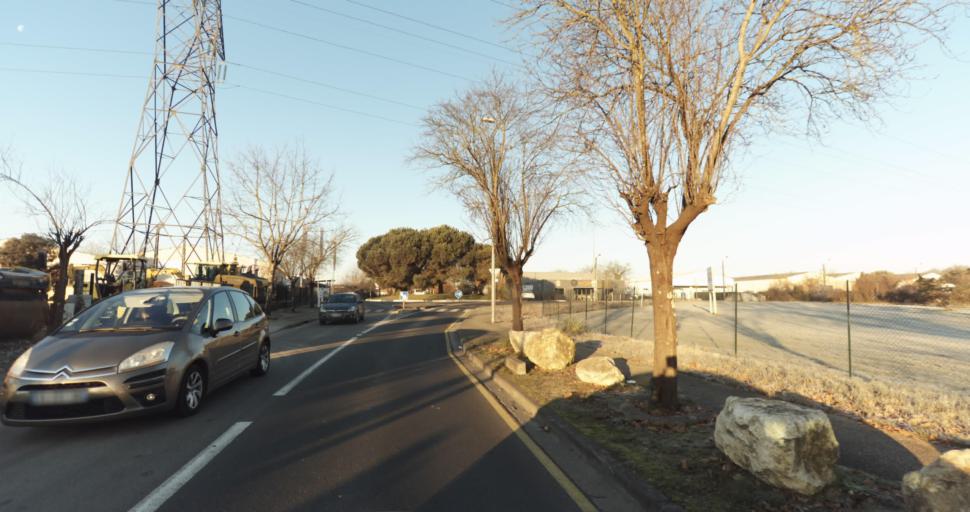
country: FR
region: Aquitaine
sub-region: Departement de la Gironde
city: Ambares-et-Lagrave
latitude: 44.9132
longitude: -0.4912
